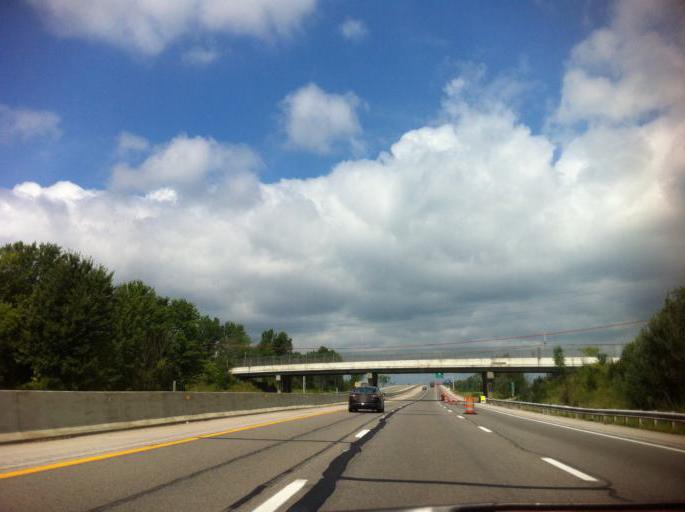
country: US
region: Ohio
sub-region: Lorain County
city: North Ridgeville
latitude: 41.3711
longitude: -81.9746
